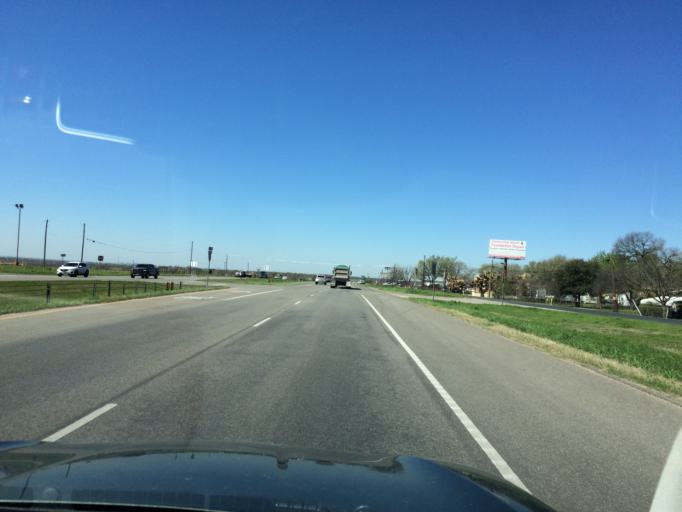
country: US
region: Texas
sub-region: Travis County
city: Garfield
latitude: 30.1870
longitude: -97.5574
